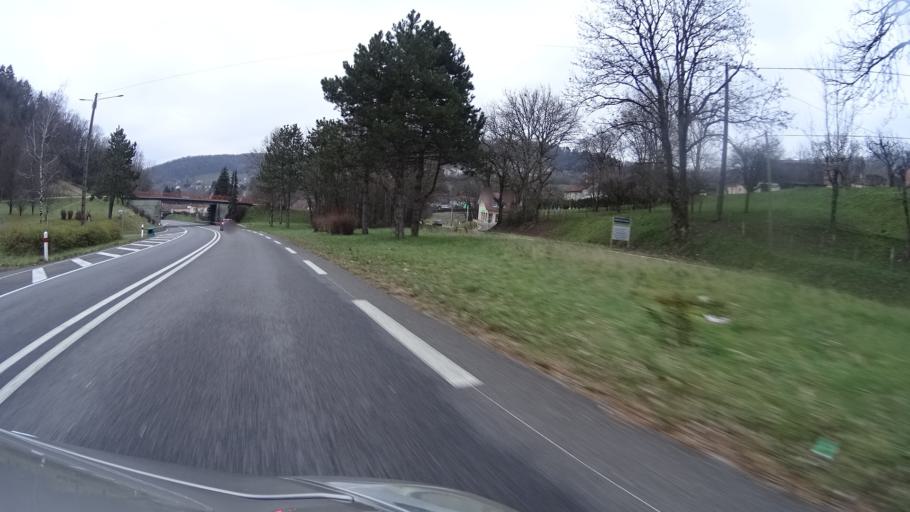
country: FR
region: Franche-Comte
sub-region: Departement du Doubs
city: Morre
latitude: 47.2236
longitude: 6.0633
